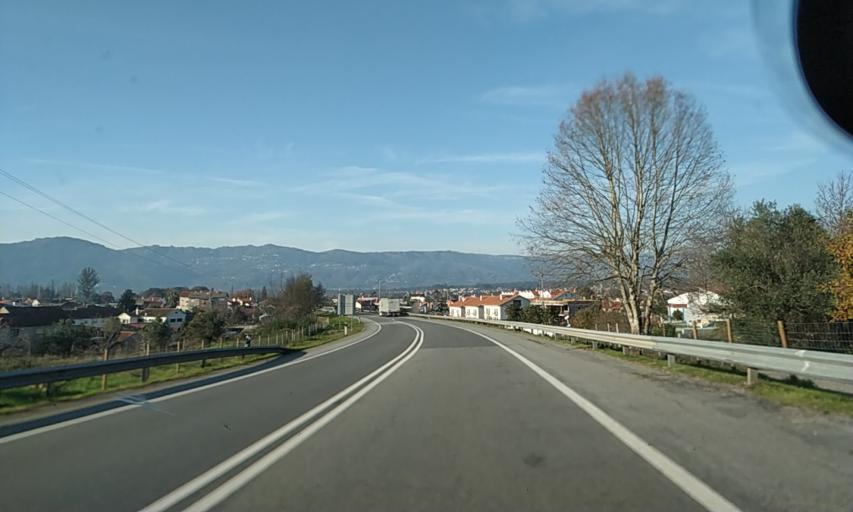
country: PT
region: Viseu
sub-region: Concelho de Tondela
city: Tondela
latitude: 40.5100
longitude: -8.0864
